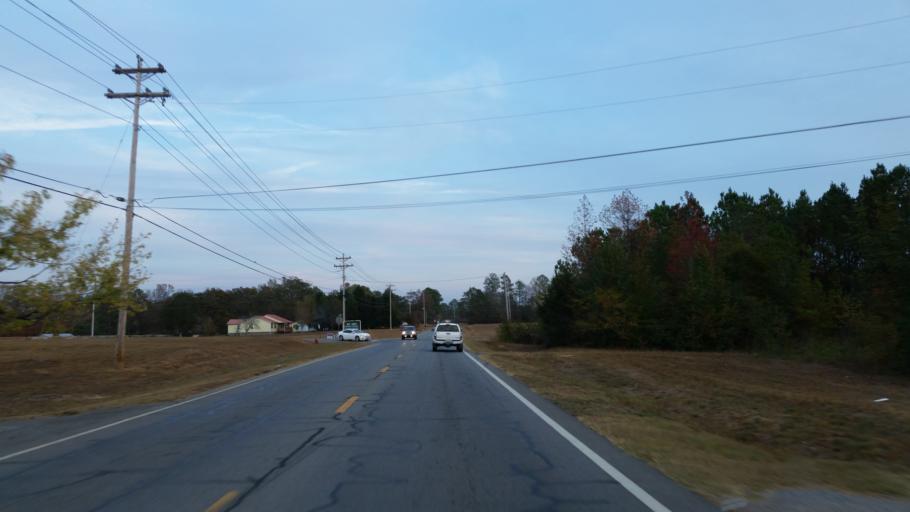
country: US
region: Georgia
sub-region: Gordon County
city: Calhoun
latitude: 34.6013
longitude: -84.9217
